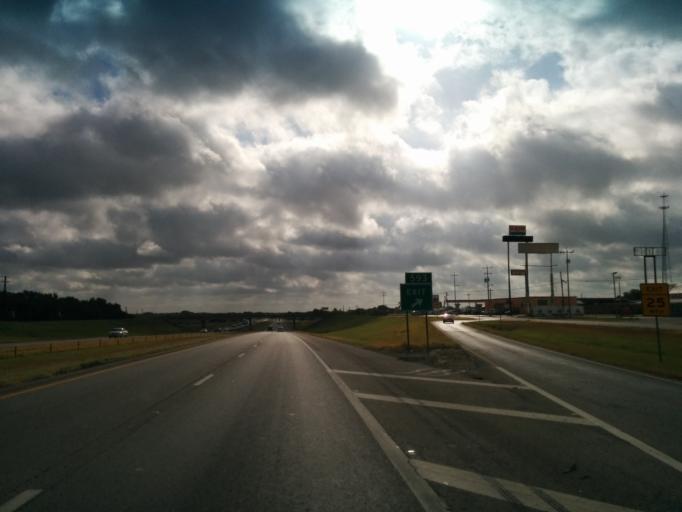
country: US
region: Texas
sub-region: Guadalupe County
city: Cibolo
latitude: 29.4966
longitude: -98.1977
